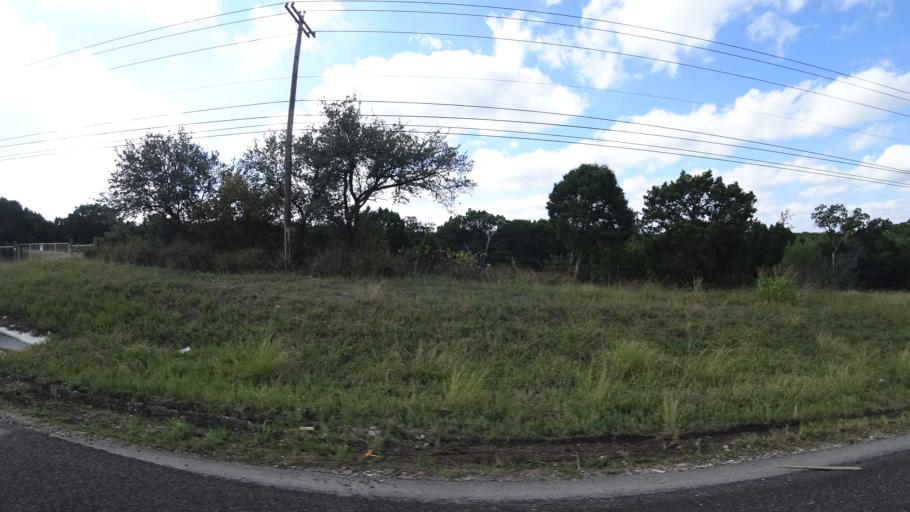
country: US
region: Texas
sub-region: Travis County
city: Barton Creek
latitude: 30.2733
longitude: -97.9132
